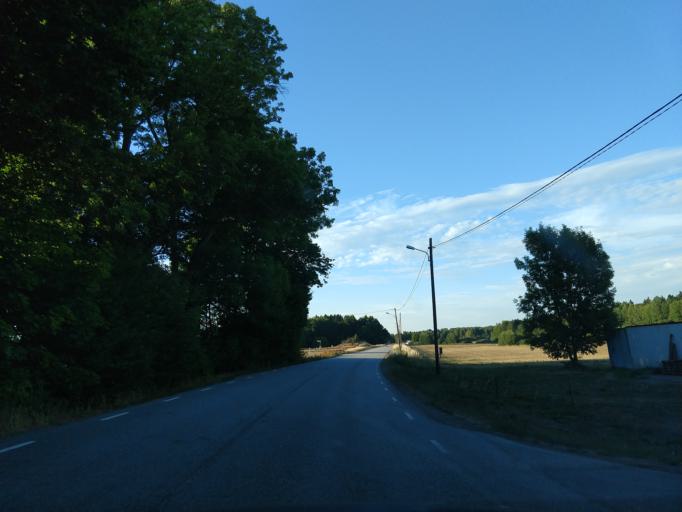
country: SE
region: Blekinge
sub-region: Ronneby Kommun
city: Brakne-Hoby
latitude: 56.2540
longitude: 15.1166
